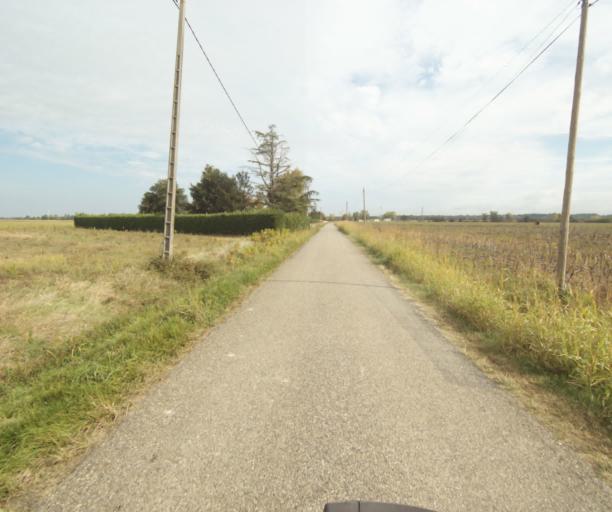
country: FR
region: Midi-Pyrenees
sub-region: Departement du Tarn-et-Garonne
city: Finhan
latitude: 43.9039
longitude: 1.2377
